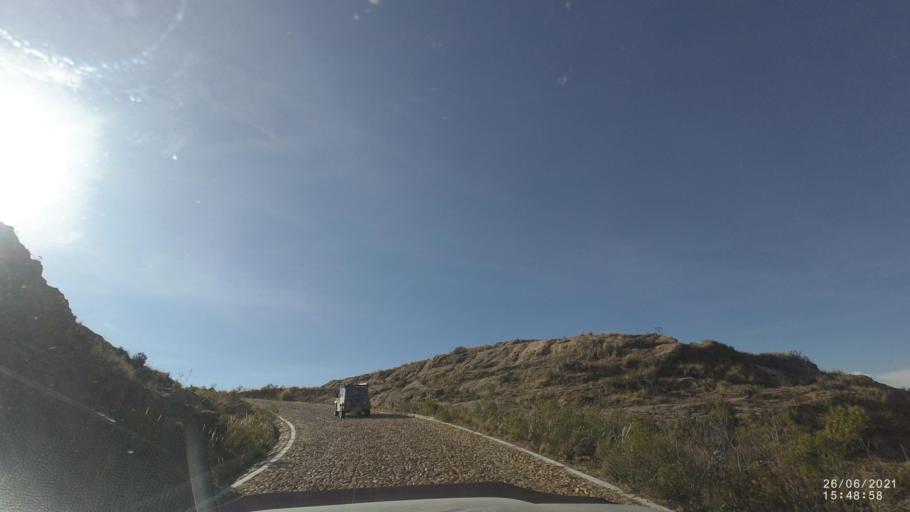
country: BO
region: Cochabamba
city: Arani
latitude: -17.8588
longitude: -65.6961
